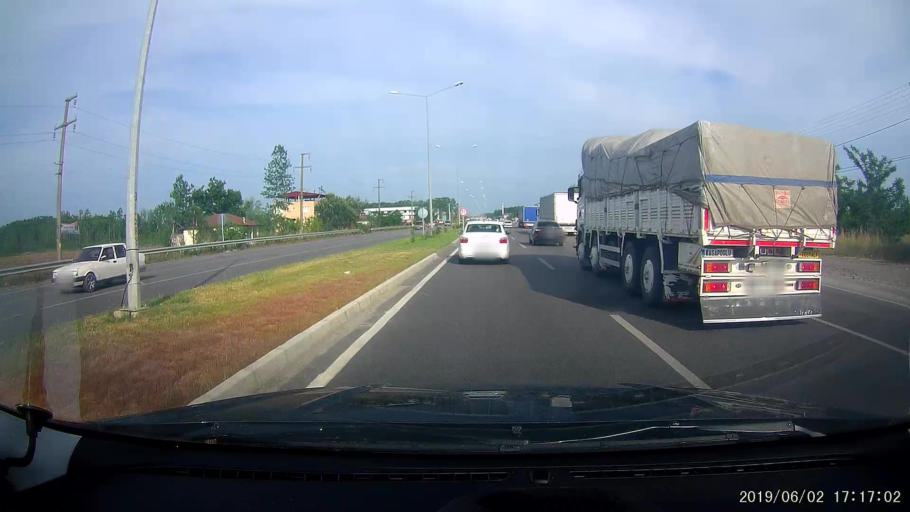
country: TR
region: Samsun
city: Dikbiyik
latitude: 41.2315
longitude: 36.5752
